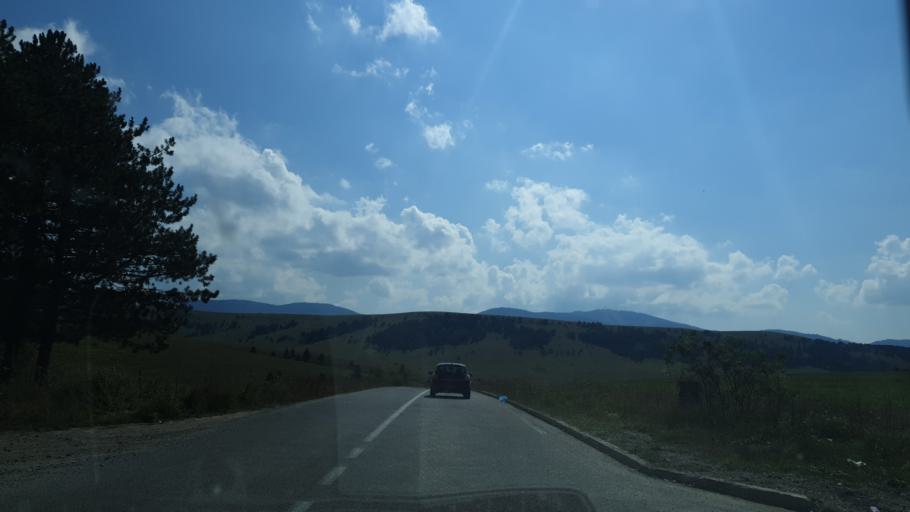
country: RS
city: Zlatibor
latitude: 43.7022
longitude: 19.6869
